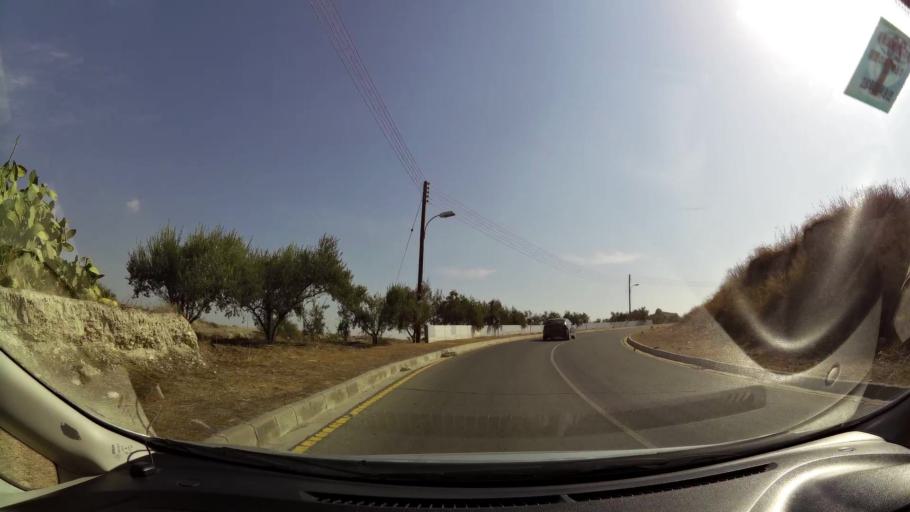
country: CY
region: Larnaka
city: Aradippou
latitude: 34.9516
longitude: 33.5743
